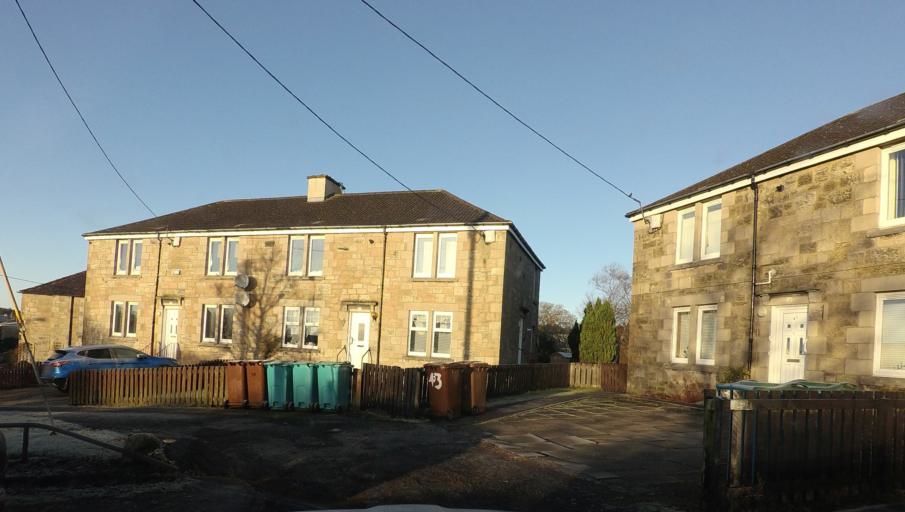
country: GB
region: Scotland
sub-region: North Lanarkshire
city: Shotts
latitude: 55.8225
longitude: -3.8021
